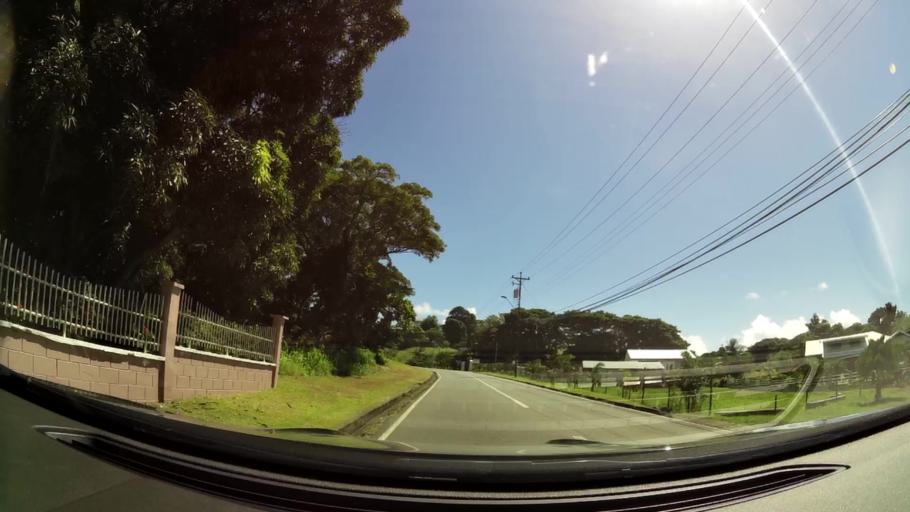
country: TT
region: Tobago
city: Scarborough
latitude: 11.1801
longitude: -60.7983
